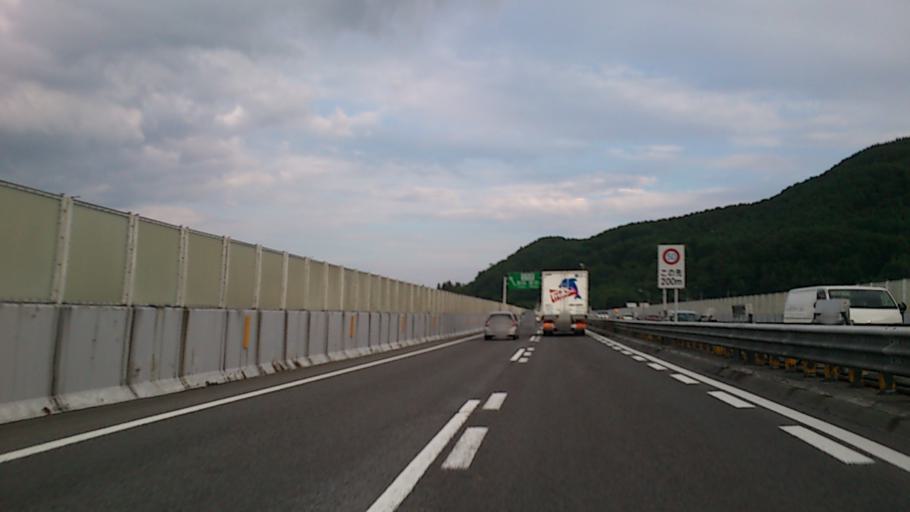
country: JP
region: Nagano
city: Okaya
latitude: 36.0564
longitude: 138.0405
